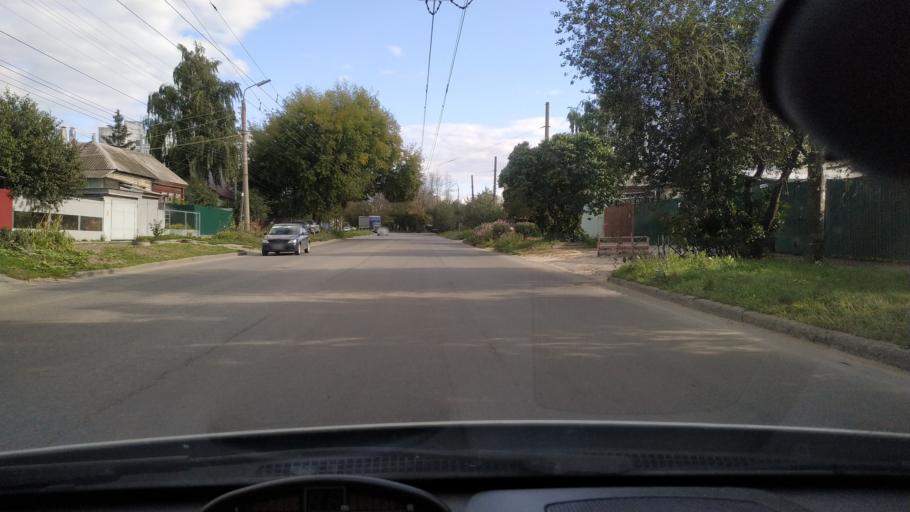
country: RU
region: Rjazan
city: Ryazan'
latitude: 54.6108
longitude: 39.6978
